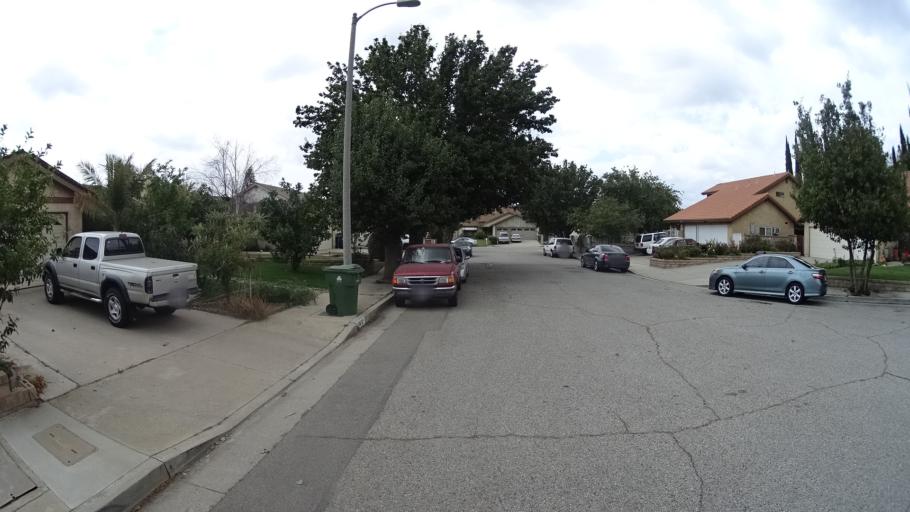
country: US
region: California
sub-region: Los Angeles County
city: San Fernando
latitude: 34.2493
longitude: -118.4506
